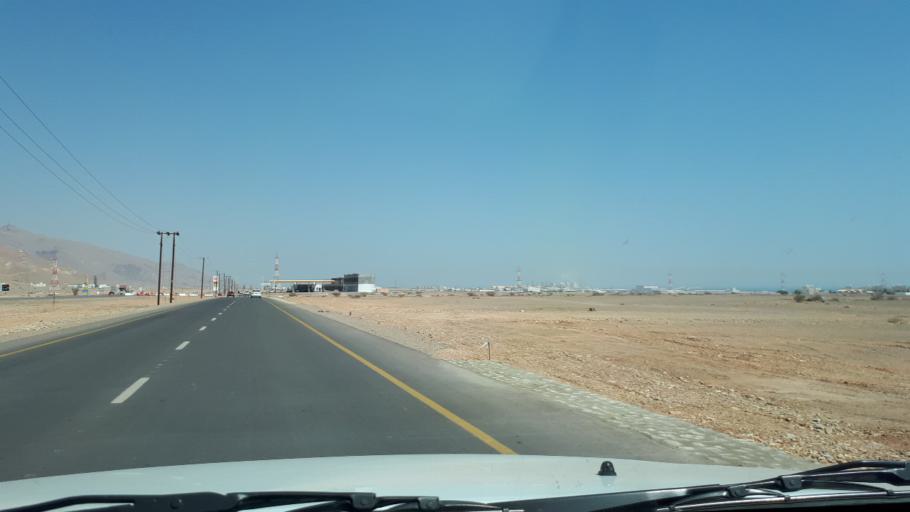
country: OM
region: Ash Sharqiyah
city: Sur
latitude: 22.5984
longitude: 59.4347
